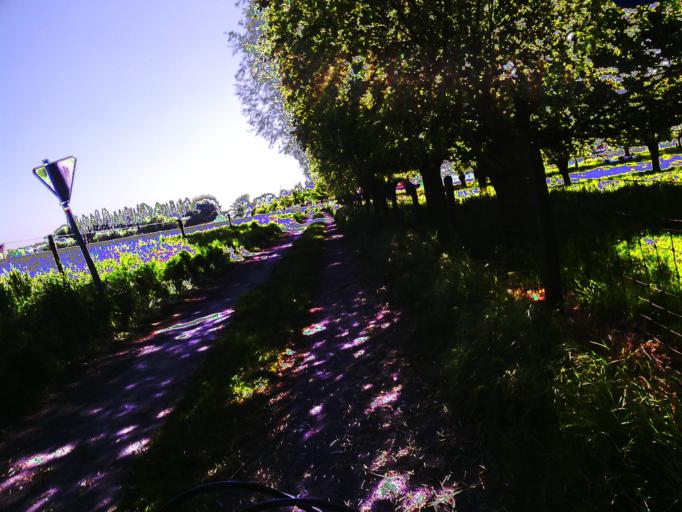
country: BE
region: Flanders
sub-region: Provincie West-Vlaanderen
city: Wevelgem
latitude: 50.7868
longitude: 3.1849
